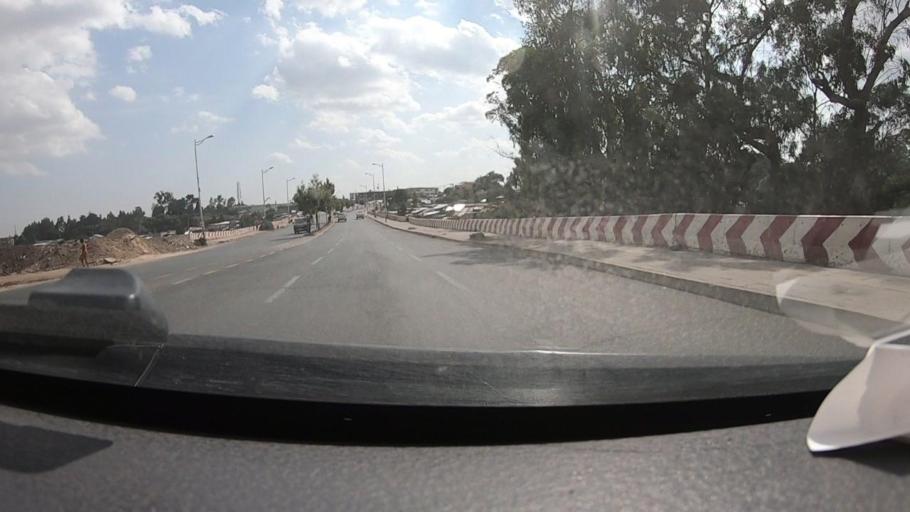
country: ET
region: Adis Abeba
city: Addis Ababa
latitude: 9.0503
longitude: 38.7704
